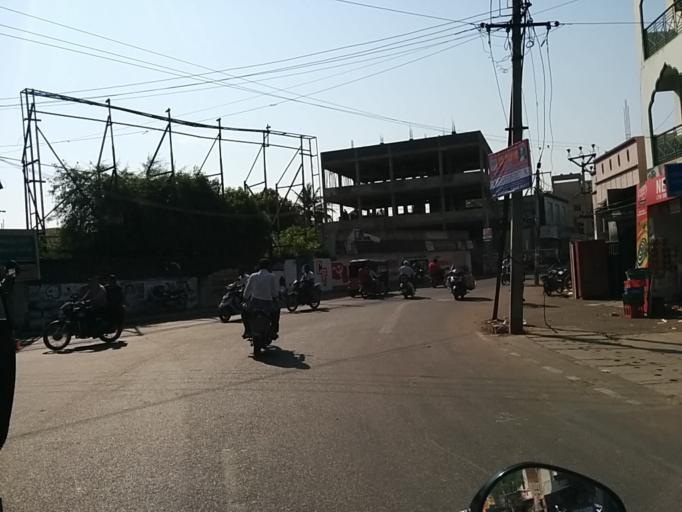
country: IN
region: Pondicherry
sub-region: Puducherry
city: Puducherry
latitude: 11.9515
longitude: 79.8309
